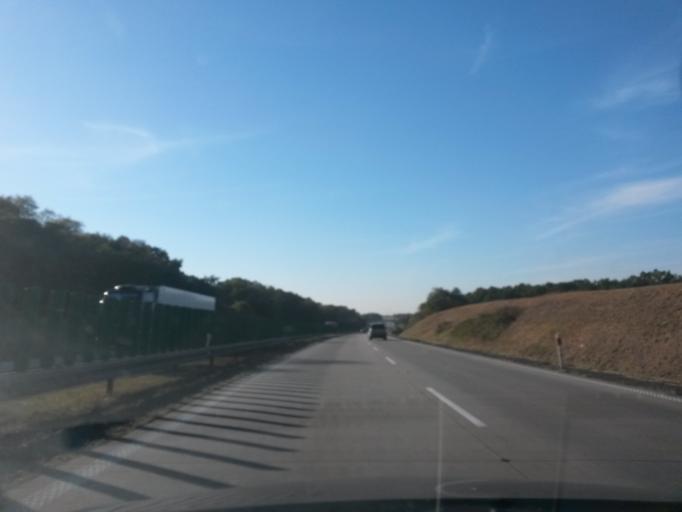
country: PL
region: Lower Silesian Voivodeship
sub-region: Powiat wroclawski
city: Katy Wroclawskie
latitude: 51.0202
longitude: 16.6887
